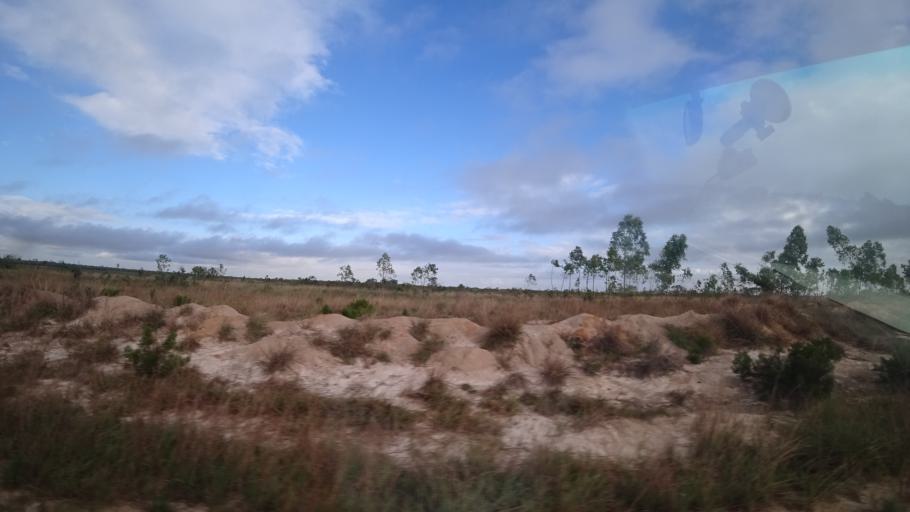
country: MZ
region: Sofala
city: Beira
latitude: -19.6248
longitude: 35.0604
